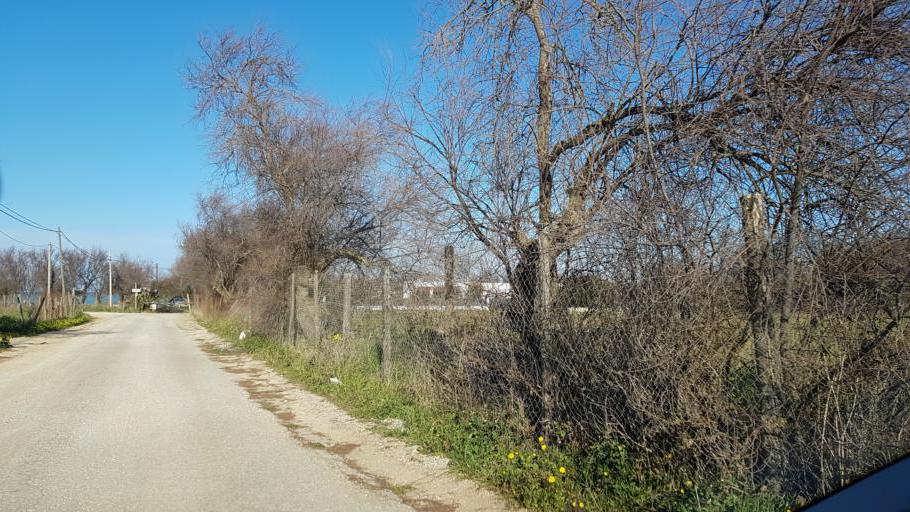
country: IT
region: Apulia
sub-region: Provincia di Brindisi
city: San Vito dei Normanni
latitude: 40.6934
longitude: 17.8267
